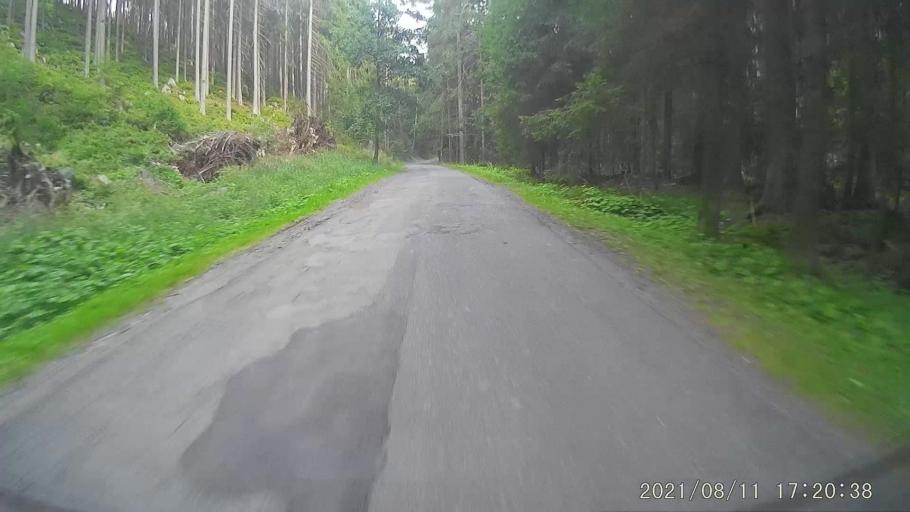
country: PL
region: Lower Silesian Voivodeship
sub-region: Powiat klodzki
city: Polanica-Zdroj
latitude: 50.3081
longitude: 16.5100
